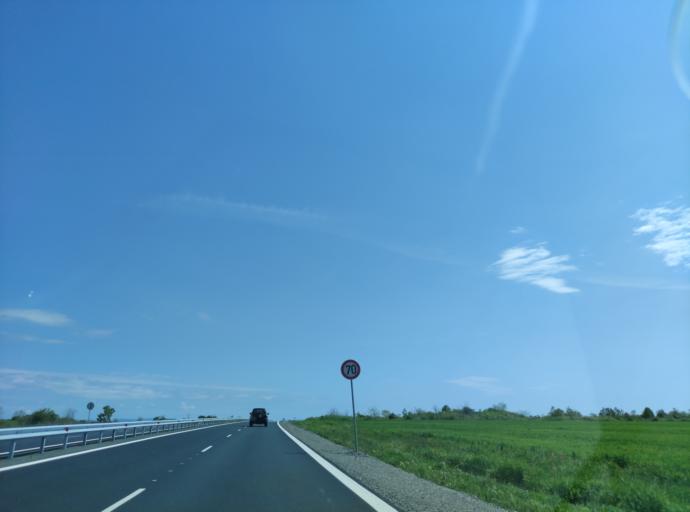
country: BG
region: Burgas
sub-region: Obshtina Pomorie
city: Pomorie
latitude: 42.5825
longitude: 27.5839
